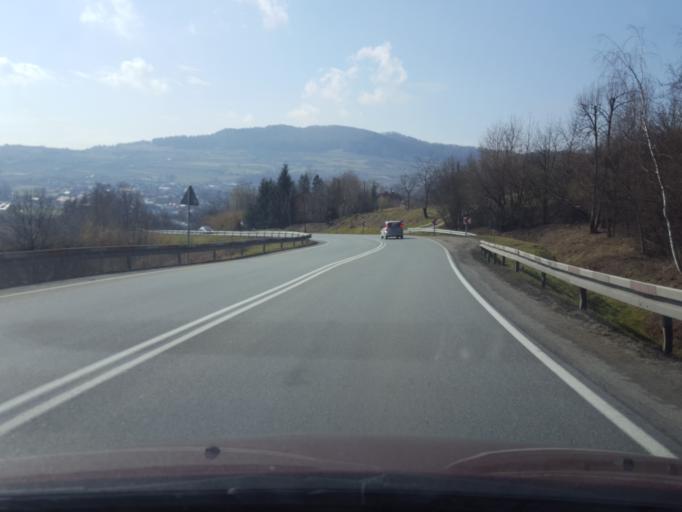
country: PL
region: Lesser Poland Voivodeship
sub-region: Powiat nowosadecki
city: Lososina Dolna
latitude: 49.7198
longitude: 20.6419
